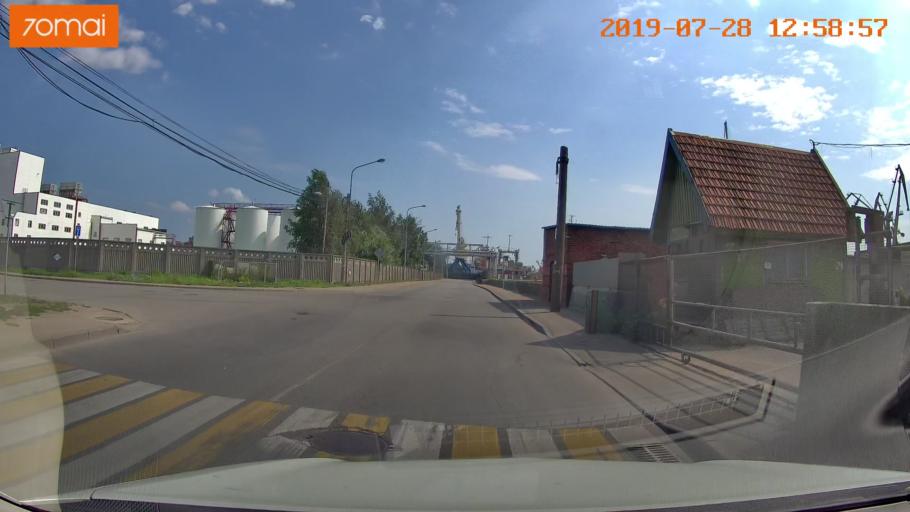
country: RU
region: Kaliningrad
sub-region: Gorod Kaliningrad
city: Kaliningrad
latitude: 54.7050
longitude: 20.4801
